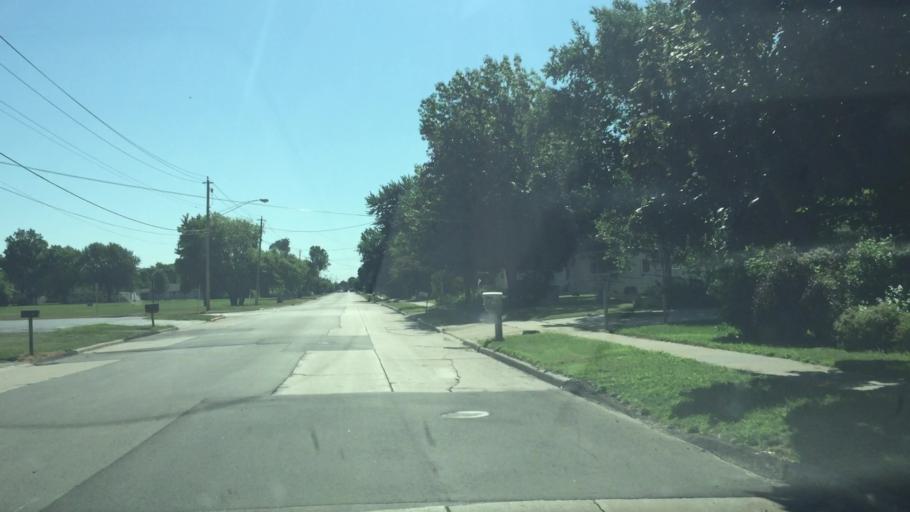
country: US
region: Wisconsin
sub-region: Winnebago County
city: Menasha
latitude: 44.2226
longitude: -88.4390
